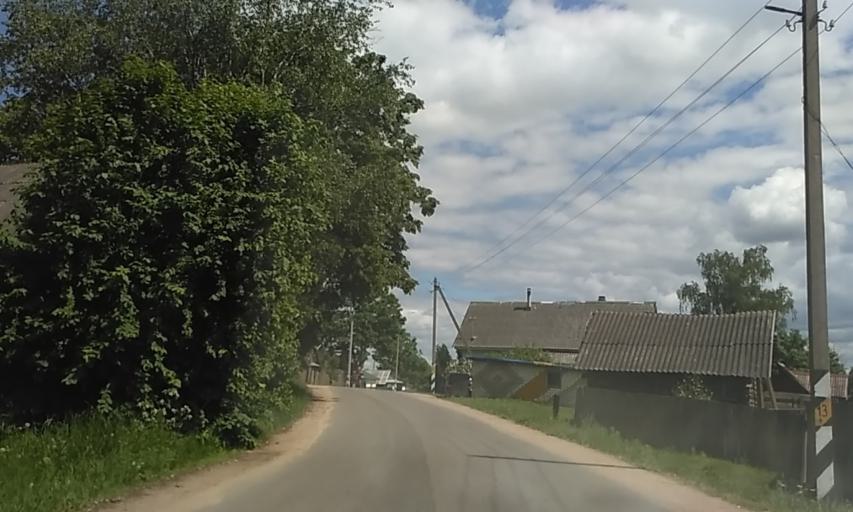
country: BY
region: Minsk
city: Krupki
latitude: 54.3514
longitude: 29.1173
